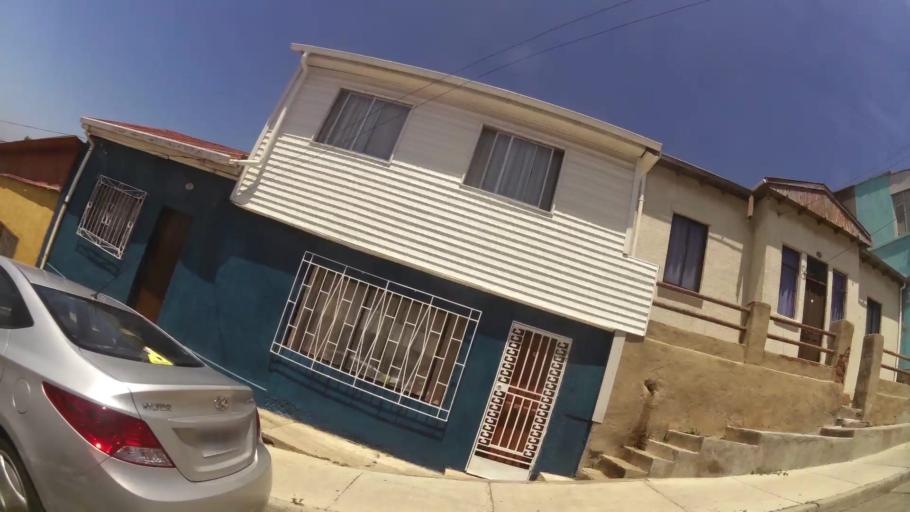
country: CL
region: Valparaiso
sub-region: Provincia de Valparaiso
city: Valparaiso
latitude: -33.0371
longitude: -71.6387
